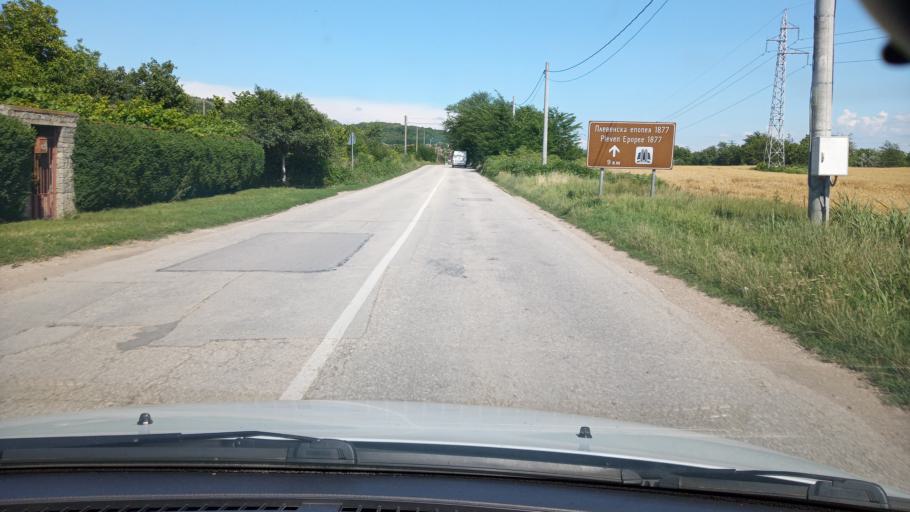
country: BG
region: Pleven
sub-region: Obshtina Dolna Mitropoliya
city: Dolna Mitropoliya
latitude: 43.4491
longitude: 24.5635
